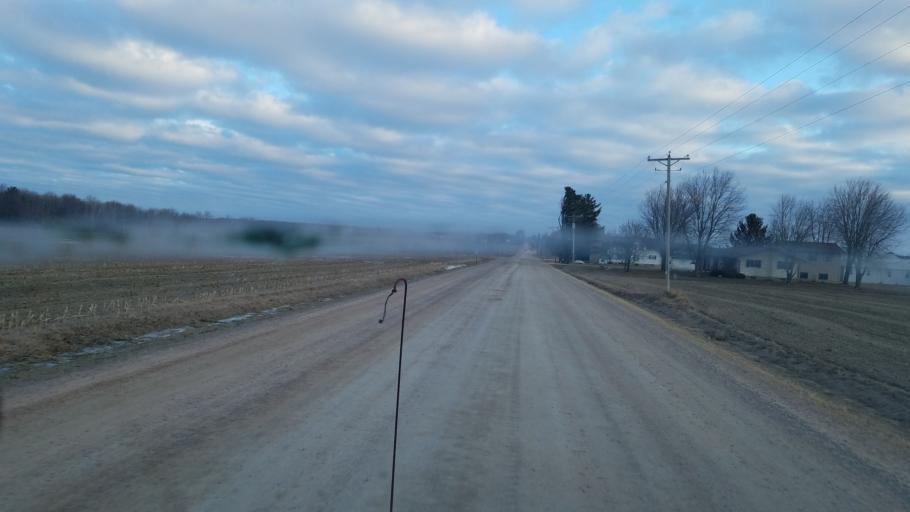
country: US
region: Wisconsin
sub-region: Clark County
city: Loyal
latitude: 44.6077
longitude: -90.4565
